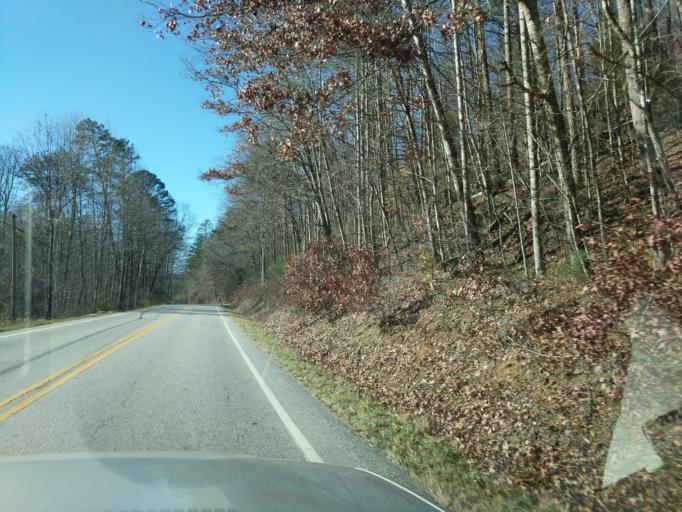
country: US
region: Georgia
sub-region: Rabun County
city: Clayton
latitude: 34.8604
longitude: -83.5037
